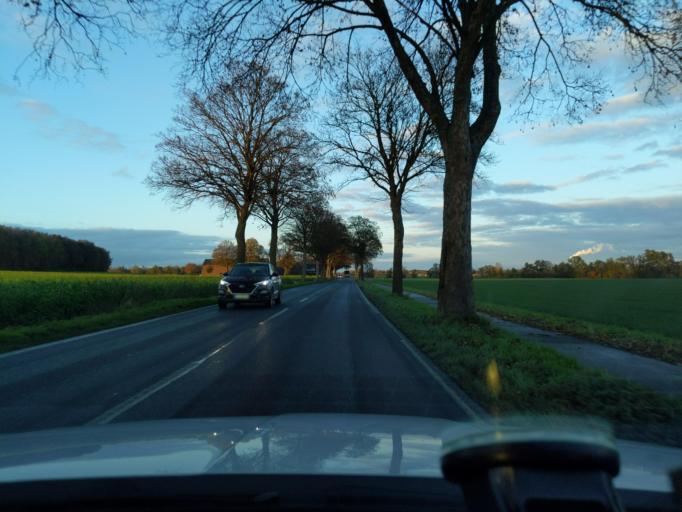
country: DE
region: North Rhine-Westphalia
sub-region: Regierungsbezirk Dusseldorf
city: Uedem
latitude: 51.6952
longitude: 6.3198
